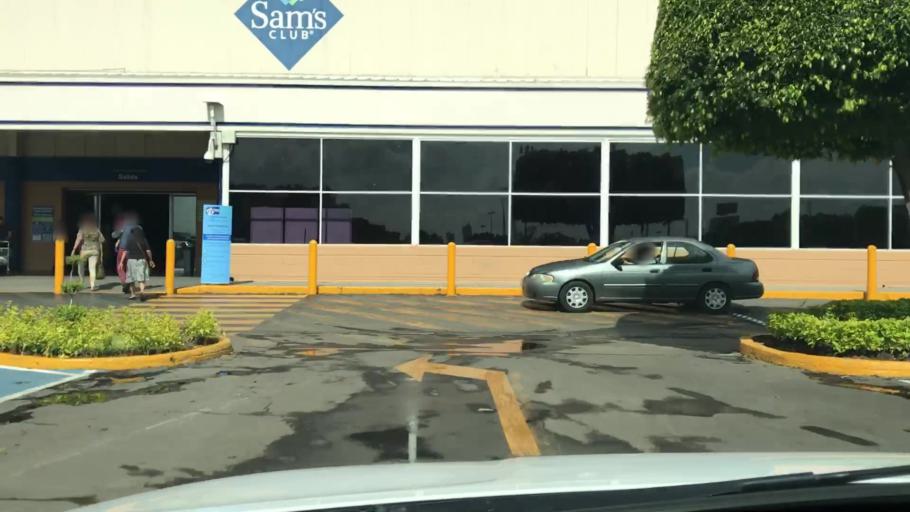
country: MX
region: Jalisco
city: Guadalajara
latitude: 20.6802
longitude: -103.4320
